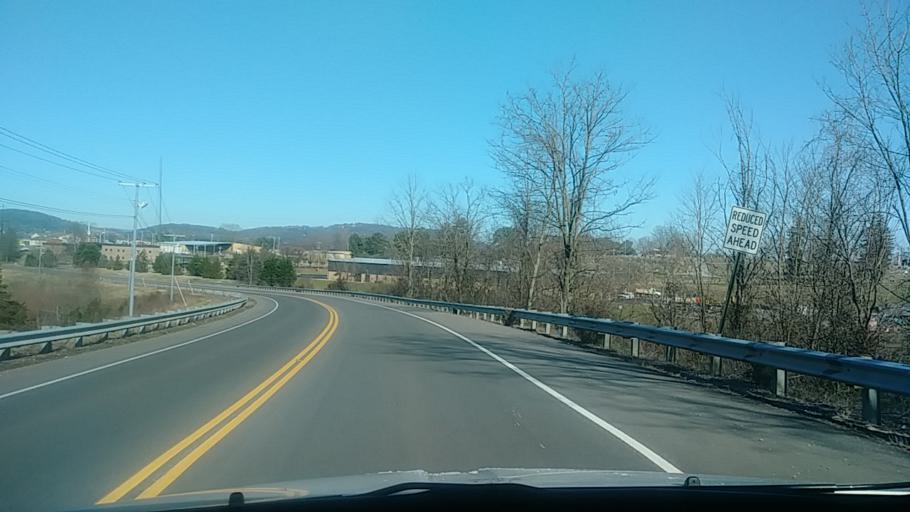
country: US
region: Tennessee
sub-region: Hamblen County
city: Morristown
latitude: 36.1921
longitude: -83.3049
